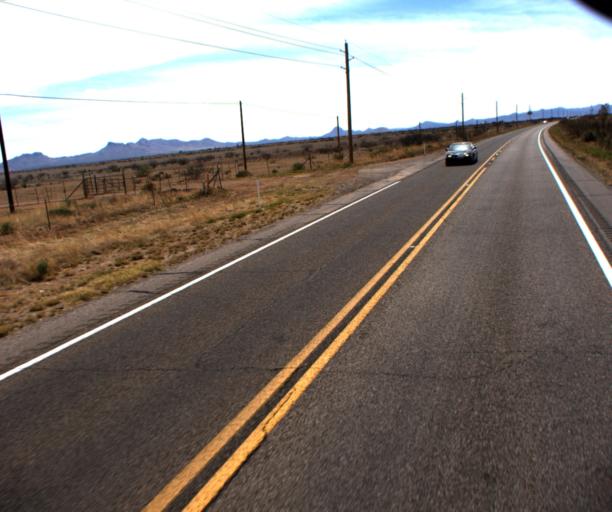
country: US
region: Arizona
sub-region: Cochise County
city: Pirtleville
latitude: 31.4342
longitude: -109.5887
